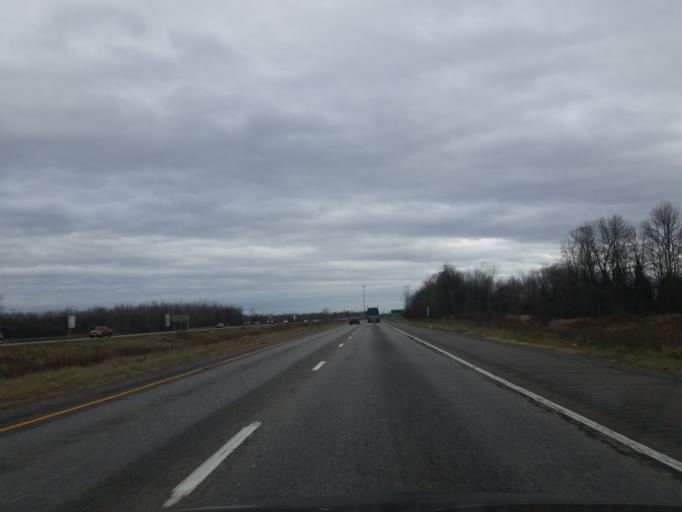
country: CA
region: Quebec
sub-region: Outaouais
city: Gatineau
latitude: 45.5101
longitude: -75.6558
